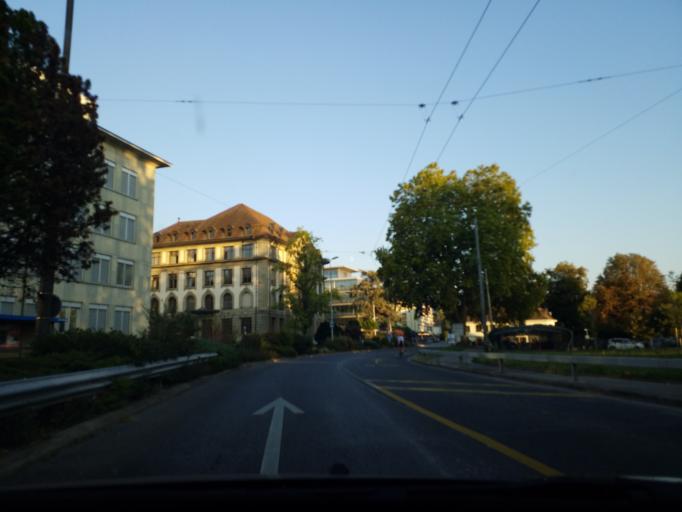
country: CH
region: Vaud
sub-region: Riviera-Pays-d'Enhaut District
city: La Tour-de-Peilz
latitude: 46.4571
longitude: 6.8529
